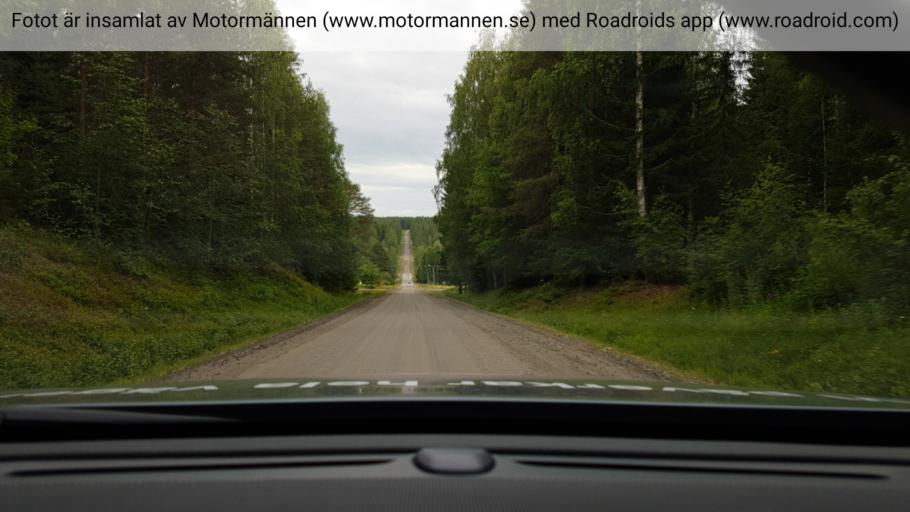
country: SE
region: Vaesterbotten
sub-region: Umea Kommun
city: Ersmark
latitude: 64.1180
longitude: 20.1093
